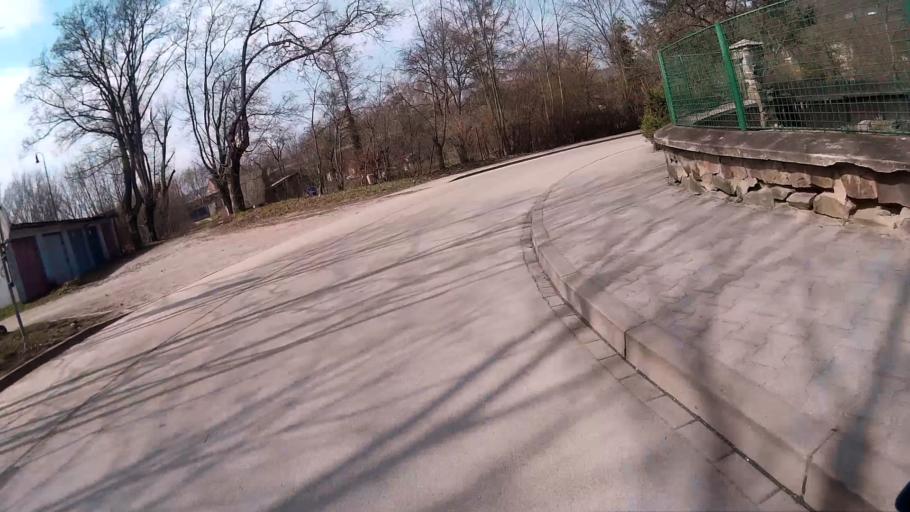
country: CZ
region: South Moravian
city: Bilovice nad Svitavou
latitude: 49.2272
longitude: 16.6540
